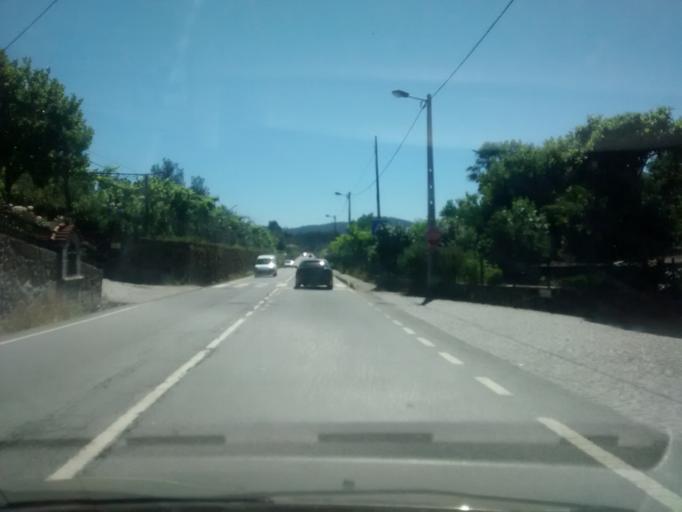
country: PT
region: Braga
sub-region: Barcelos
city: Galegos
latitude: 41.5282
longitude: -8.5608
